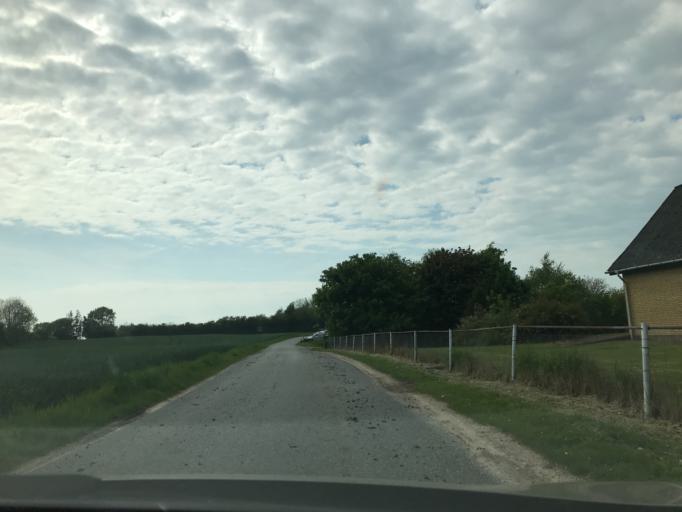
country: DK
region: South Denmark
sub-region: Middelfart Kommune
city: Ejby
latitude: 55.3546
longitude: 9.8978
